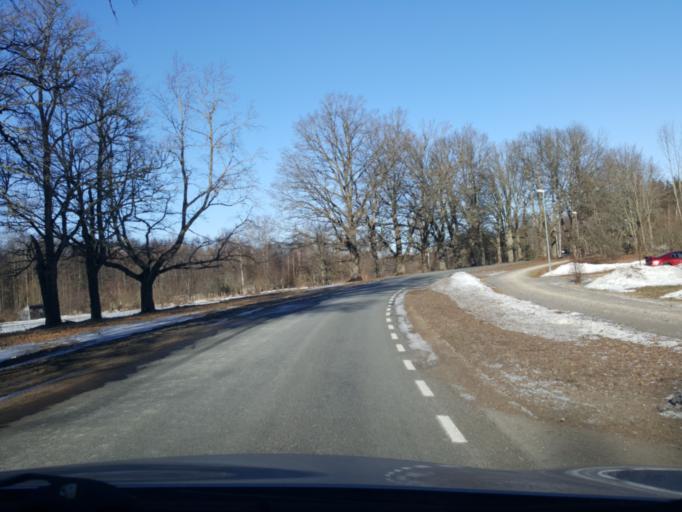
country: EE
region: Viljandimaa
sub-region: Vohma linn
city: Vohma
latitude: 58.5564
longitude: 25.5560
